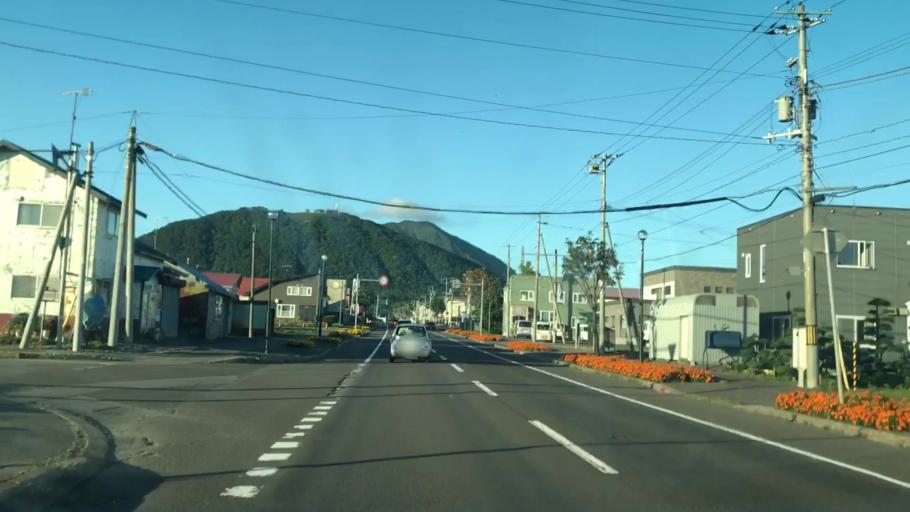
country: JP
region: Hokkaido
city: Niseko Town
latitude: 42.7324
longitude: 140.8722
